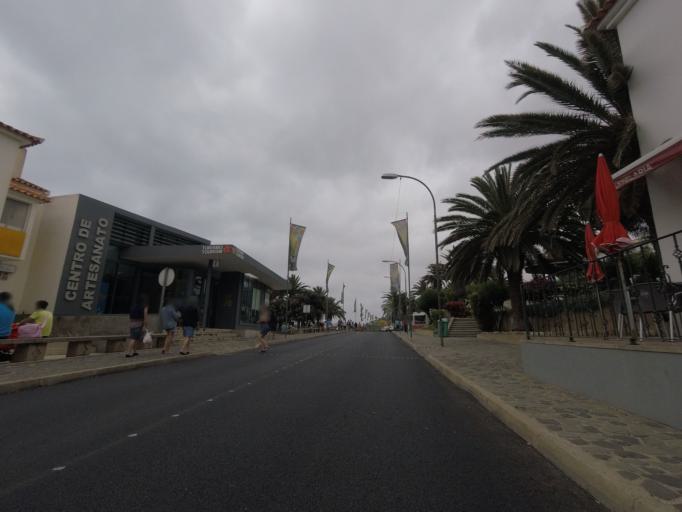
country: PT
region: Madeira
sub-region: Porto Santo
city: Vila de Porto Santo
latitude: 33.0587
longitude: -16.3346
